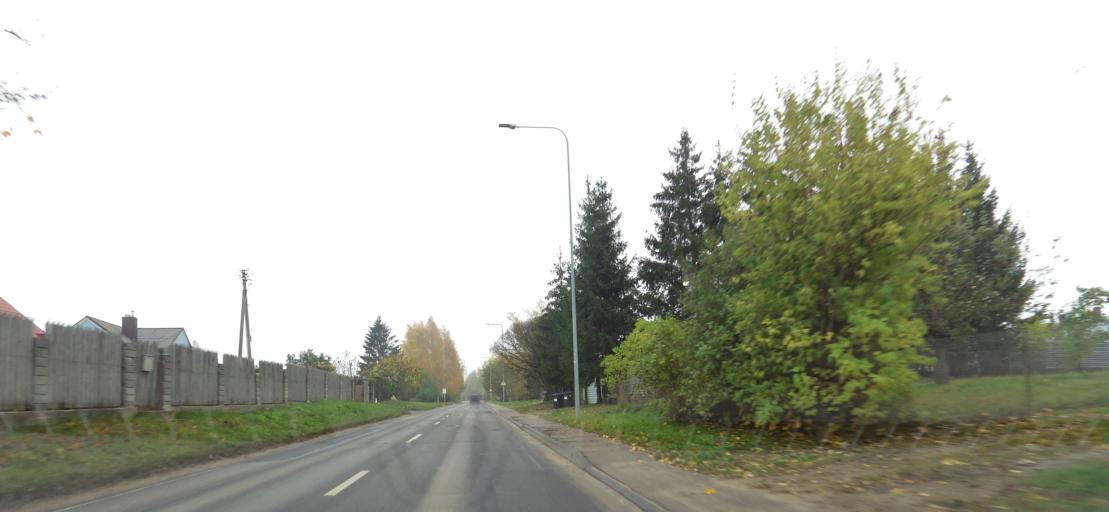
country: LT
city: Skaidiskes
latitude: 54.6596
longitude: 25.3617
